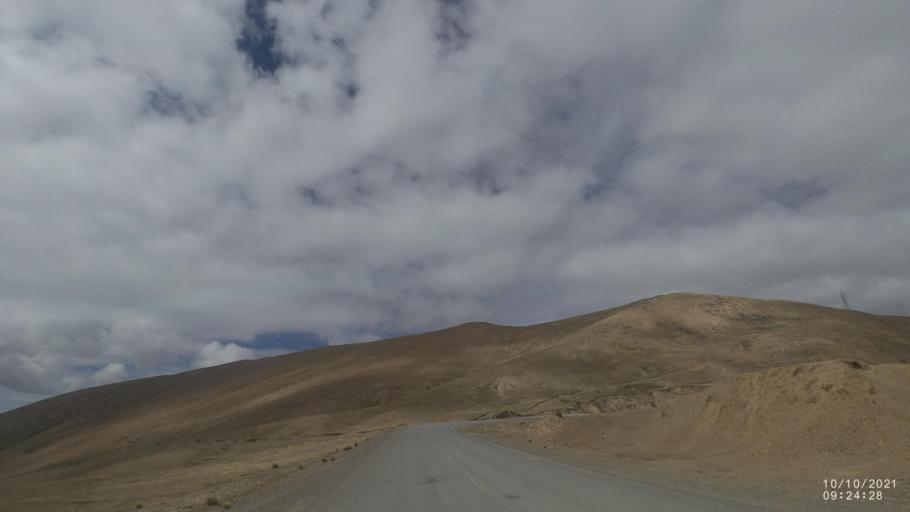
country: BO
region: La Paz
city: Quime
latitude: -17.0898
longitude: -67.3093
